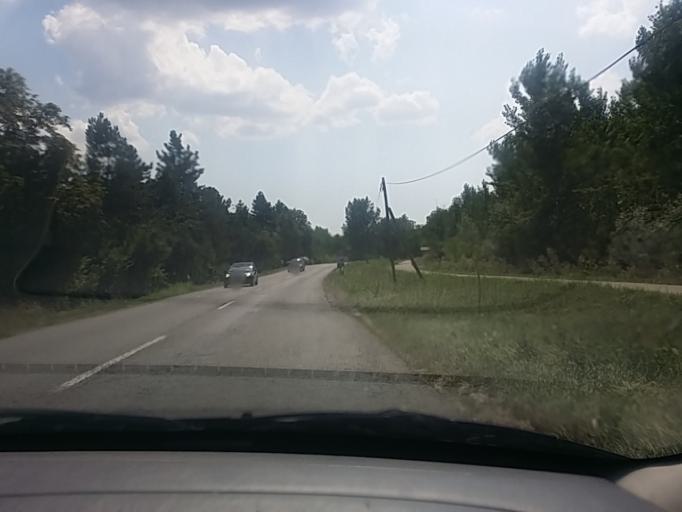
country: HU
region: Tolna
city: Dombovar
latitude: 46.3578
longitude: 18.1262
